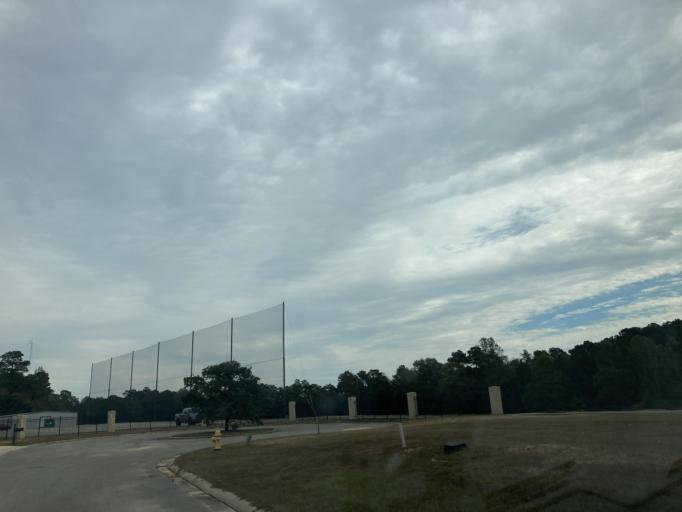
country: US
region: Mississippi
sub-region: Lamar County
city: West Hattiesburg
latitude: 31.3221
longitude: -89.3963
